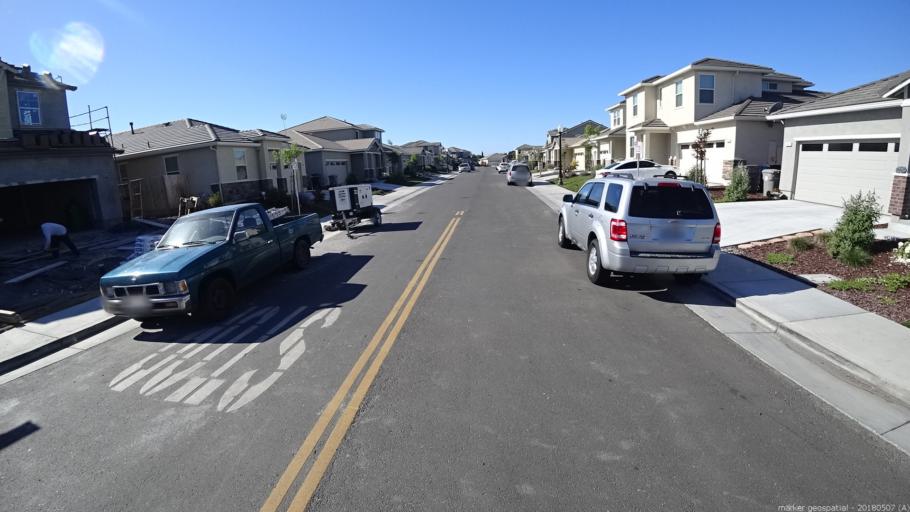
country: US
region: California
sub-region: Sacramento County
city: Rio Linda
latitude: 38.6767
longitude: -121.4939
